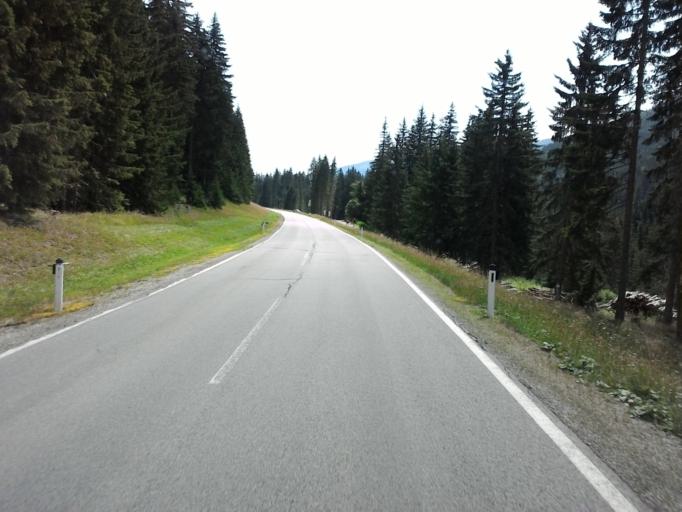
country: AT
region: Tyrol
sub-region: Politischer Bezirk Lienz
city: Obertilliach
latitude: 46.7103
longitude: 12.5825
